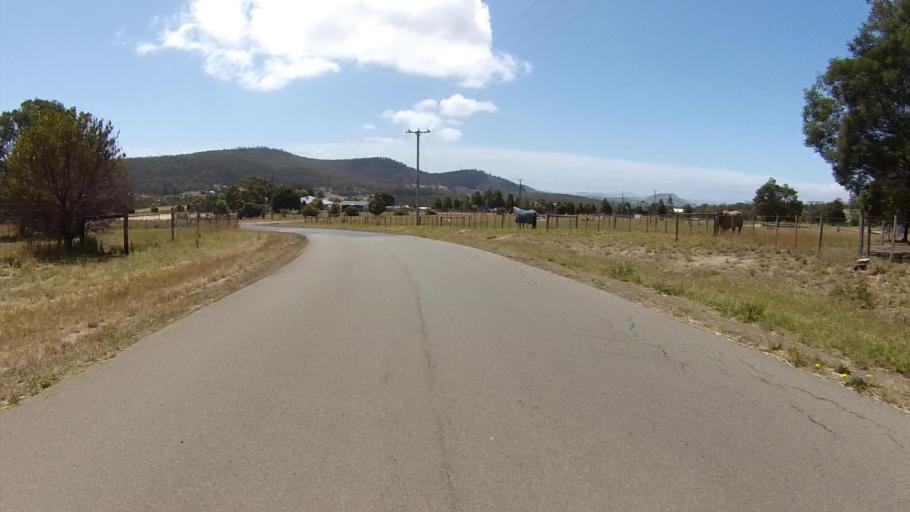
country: AU
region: Tasmania
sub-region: Clarence
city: Sandford
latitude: -42.9578
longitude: 147.4828
